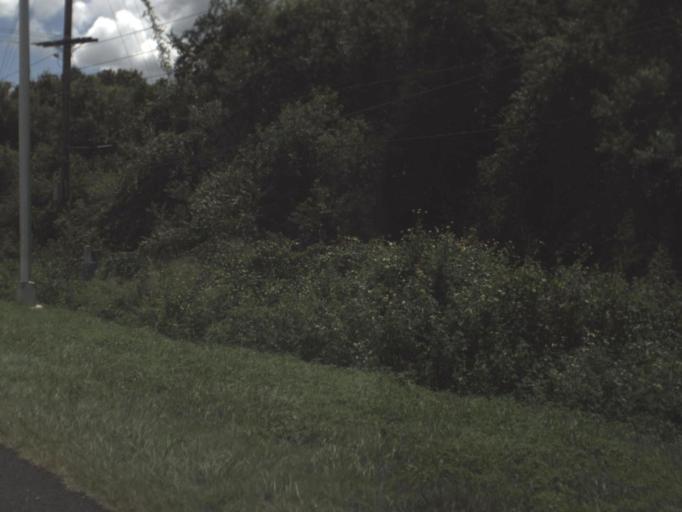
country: US
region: Florida
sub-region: Polk County
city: Lake Wales
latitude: 27.9018
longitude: -81.6083
